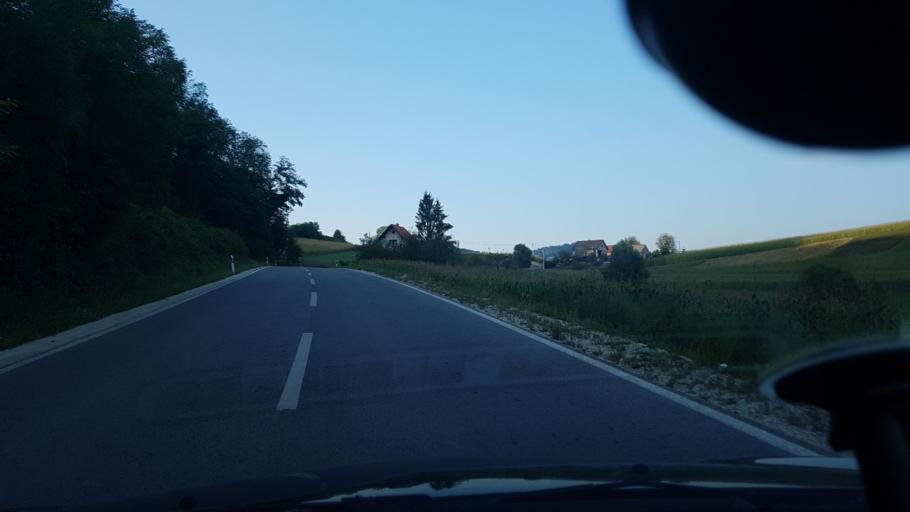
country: HR
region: Krapinsko-Zagorska
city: Pregrada
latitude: 46.1551
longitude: 15.7917
